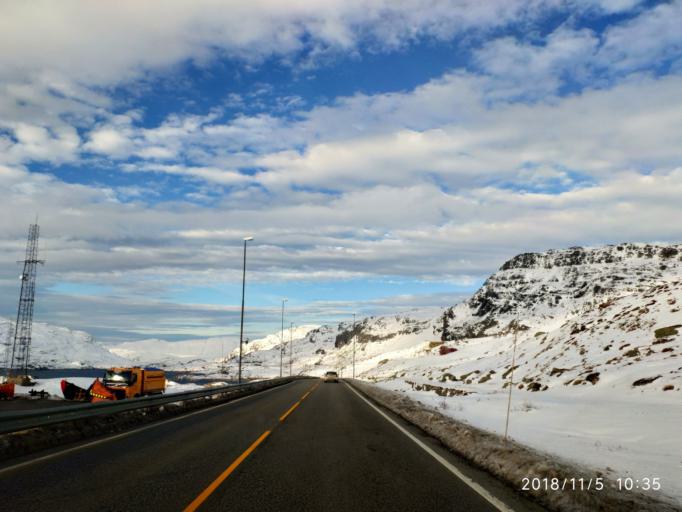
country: NO
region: Aust-Agder
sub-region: Bykle
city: Hovden
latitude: 59.8400
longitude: 6.9848
